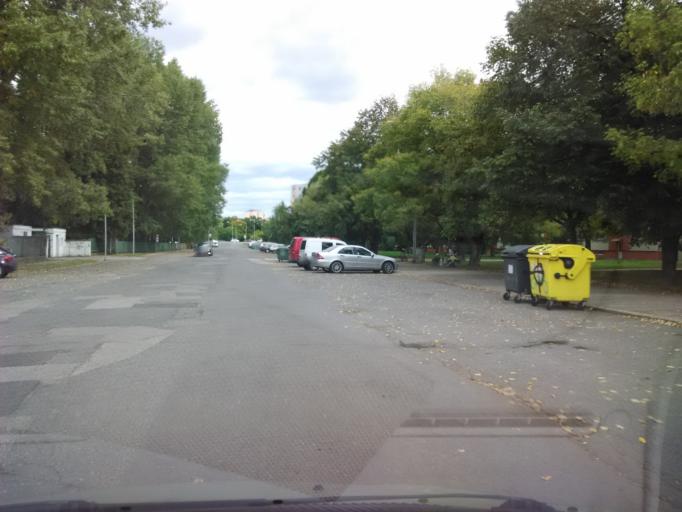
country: SK
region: Nitriansky
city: Levice
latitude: 48.2187
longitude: 18.5954
